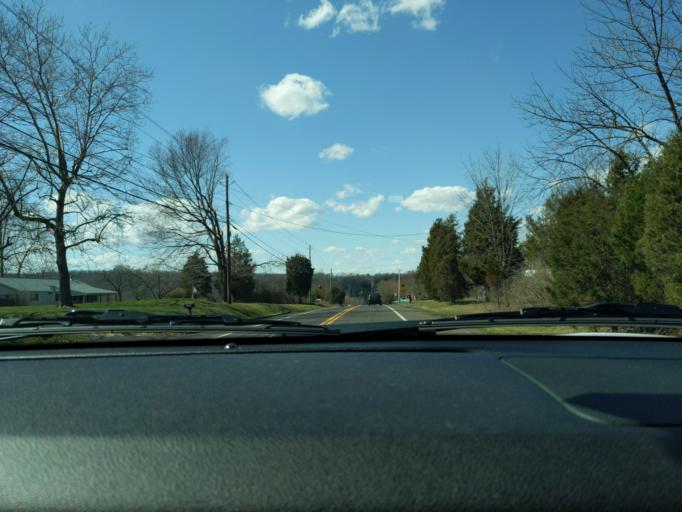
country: US
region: Pennsylvania
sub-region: Bucks County
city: Perkasie
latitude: 40.4109
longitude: -75.2645
